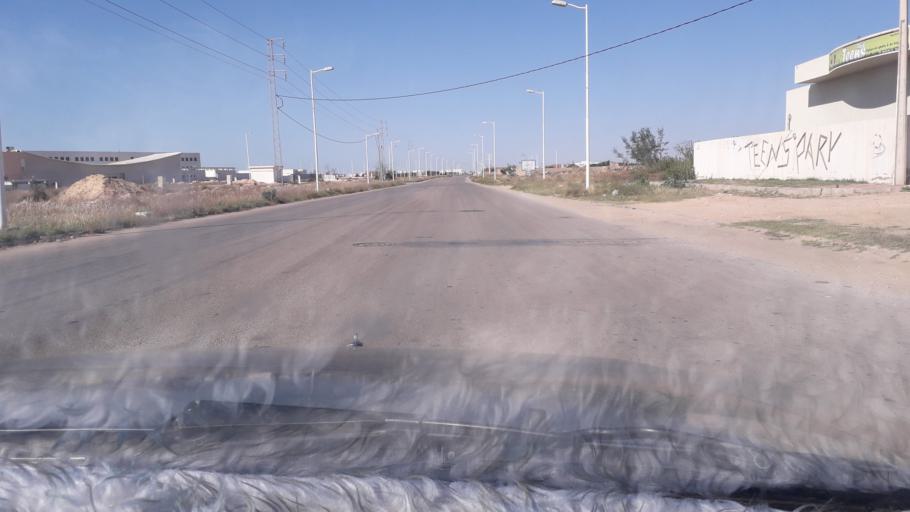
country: TN
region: Safaqis
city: Al Qarmadah
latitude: 34.8410
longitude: 10.7542
